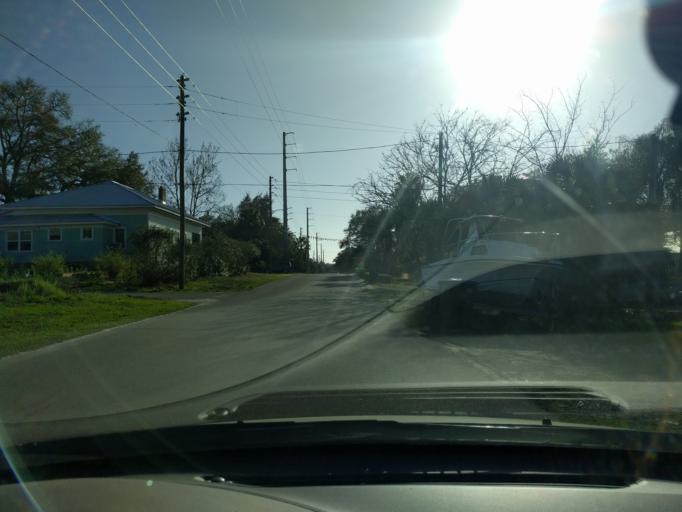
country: US
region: Florida
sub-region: Franklin County
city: Apalachicola
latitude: 29.7270
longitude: -84.9871
